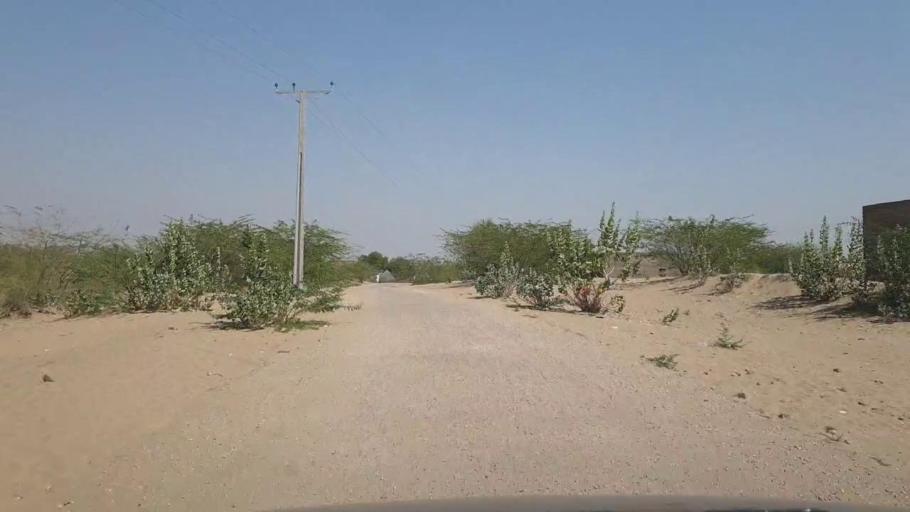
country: PK
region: Sindh
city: Chor
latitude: 25.5692
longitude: 70.1860
